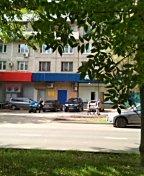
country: RU
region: Moskovskaya
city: Izmaylovo
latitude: 55.7922
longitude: 37.8059
